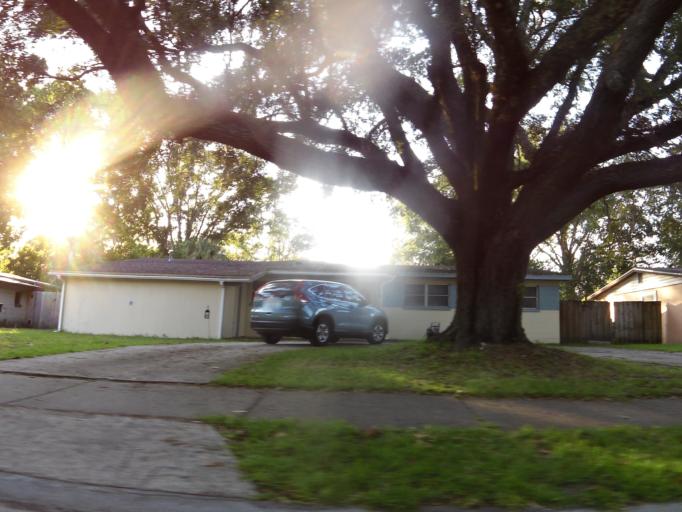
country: US
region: Florida
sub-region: Duval County
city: Jacksonville
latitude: 30.2362
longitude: -81.6111
